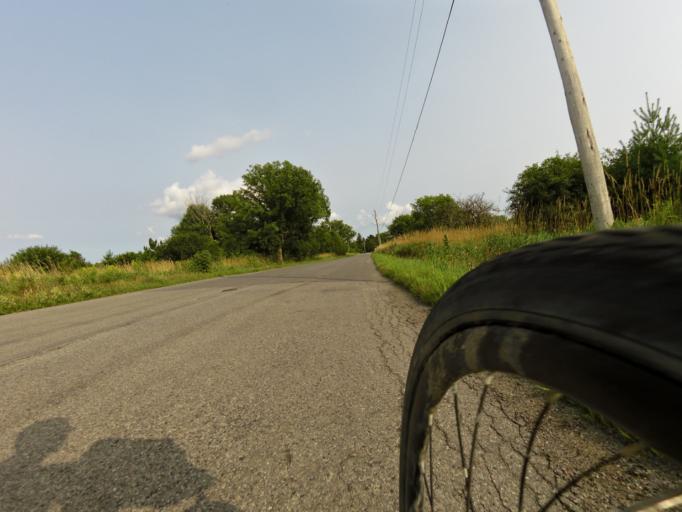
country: CA
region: Ontario
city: Quinte West
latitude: 44.0558
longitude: -77.6416
